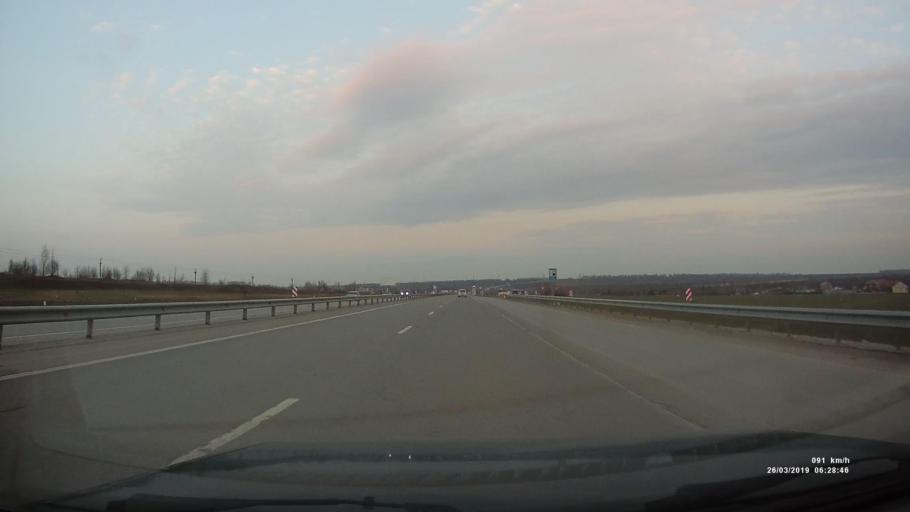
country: RU
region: Rostov
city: Krym
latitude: 47.2662
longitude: 39.5862
